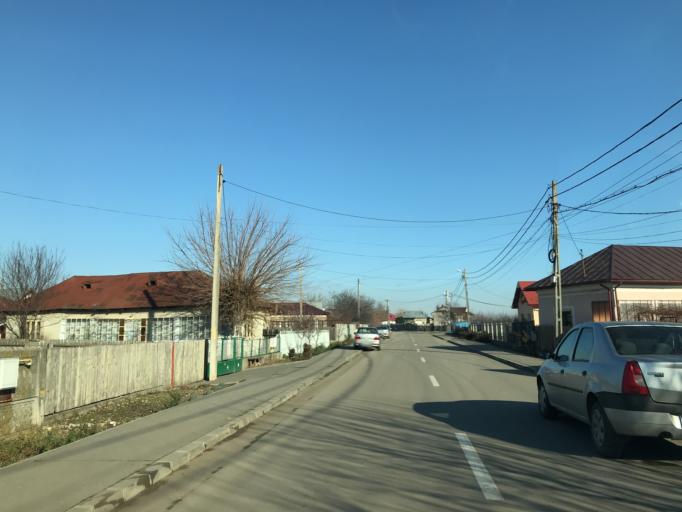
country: RO
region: Olt
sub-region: Municipiul Slatina
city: Slatina
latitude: 44.4549
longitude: 24.3727
